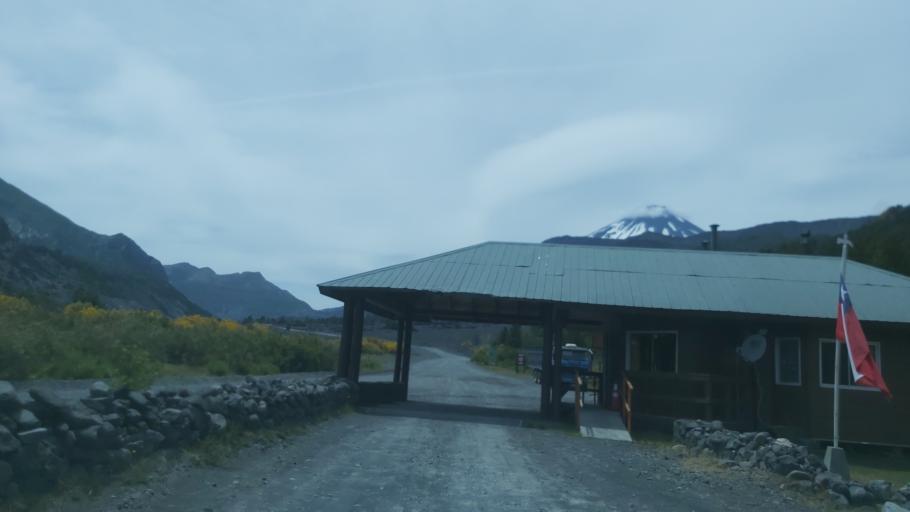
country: AR
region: Neuquen
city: Andacollo
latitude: -37.3983
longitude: -71.4402
